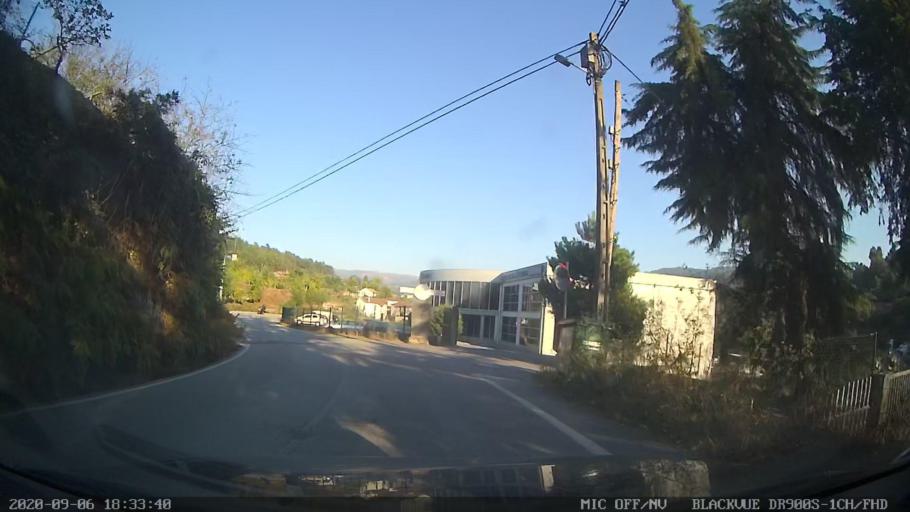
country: PT
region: Porto
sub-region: Amarante
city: Amarante
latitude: 41.2574
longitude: -8.0558
